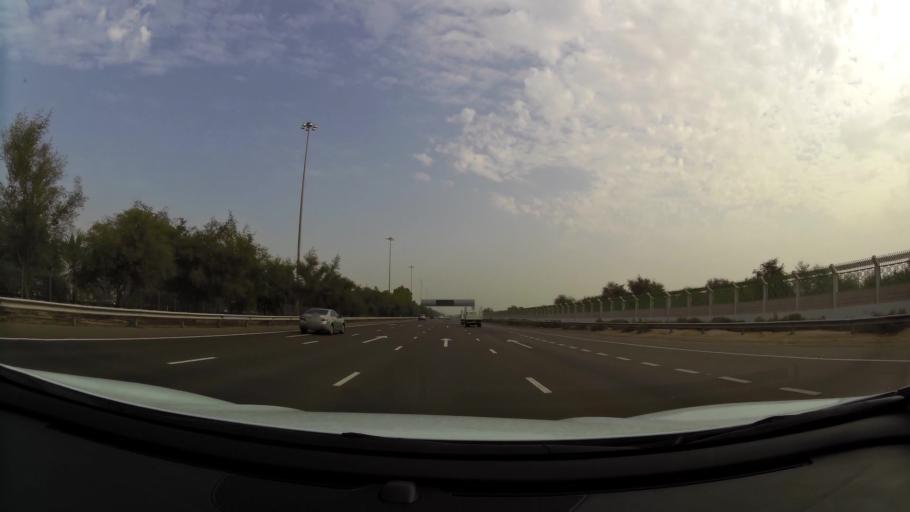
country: AE
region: Abu Dhabi
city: Abu Dhabi
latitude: 24.5862
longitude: 54.7015
